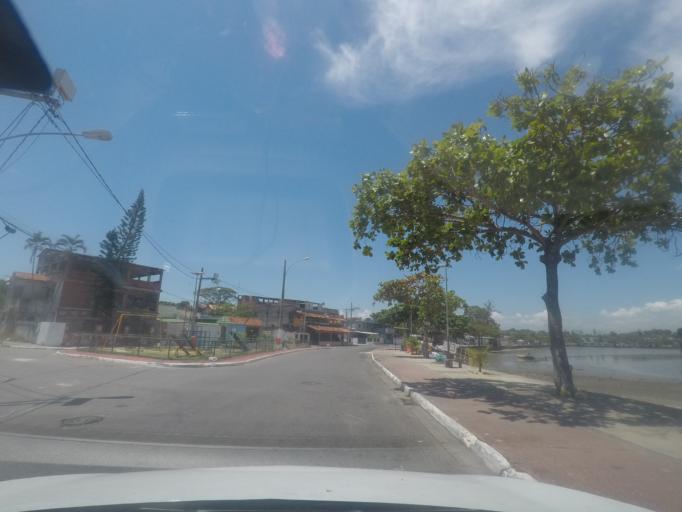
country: BR
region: Rio de Janeiro
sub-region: Itaguai
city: Itaguai
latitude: -22.9888
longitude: -43.6891
